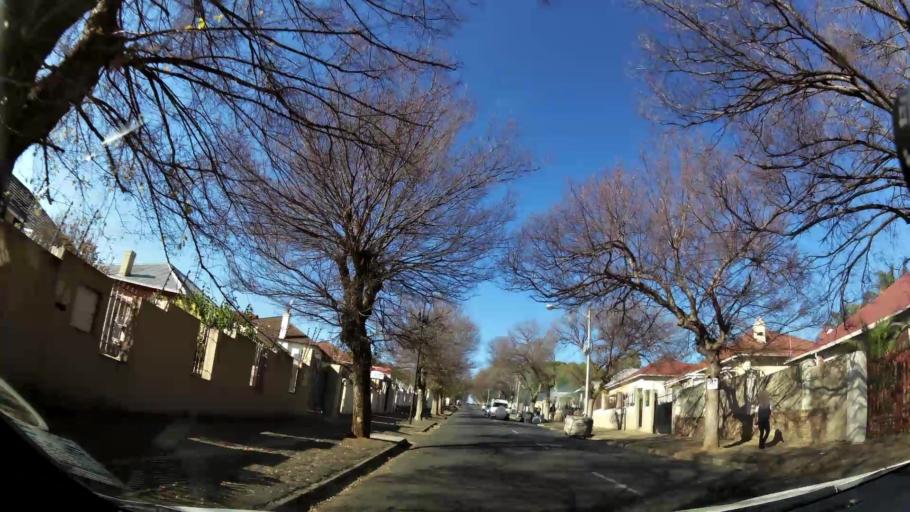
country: ZA
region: Gauteng
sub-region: City of Johannesburg Metropolitan Municipality
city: Johannesburg
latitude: -26.1964
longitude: 28.0971
